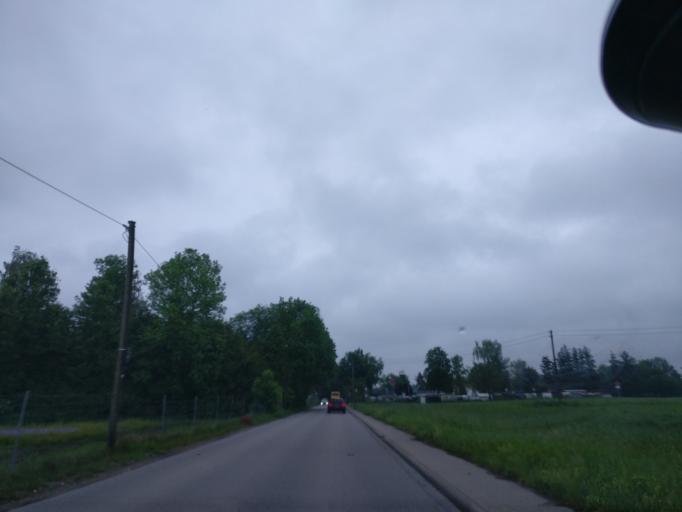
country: DE
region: Bavaria
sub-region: Upper Bavaria
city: Grobenzell
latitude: 48.2002
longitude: 11.4088
